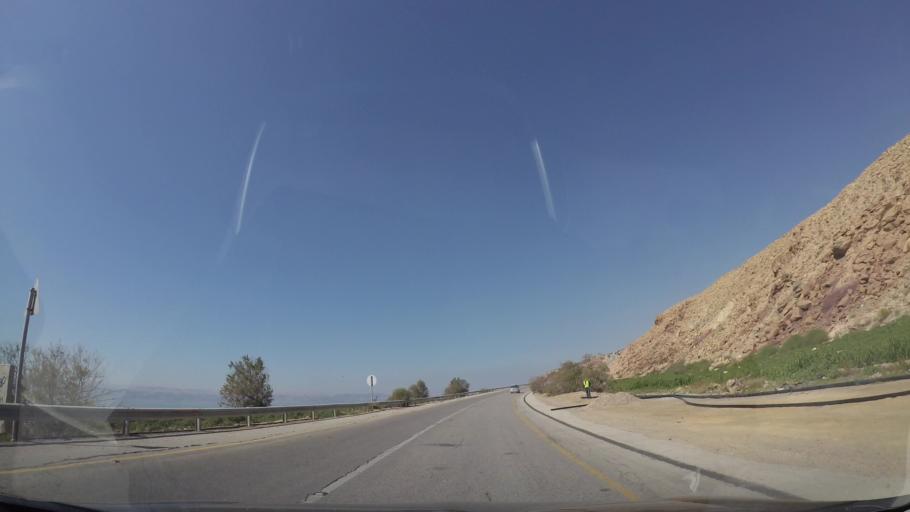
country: JO
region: Madaba
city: Madaba
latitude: 31.5525
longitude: 35.5552
